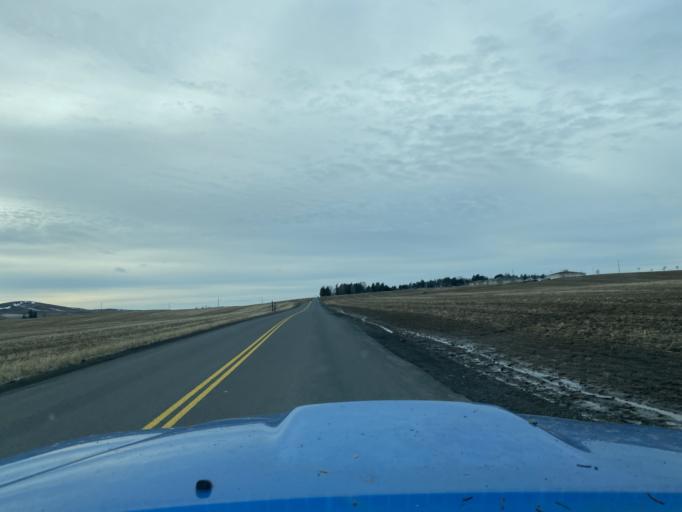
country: US
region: Idaho
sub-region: Latah County
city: Moscow
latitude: 46.7156
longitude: -116.9745
